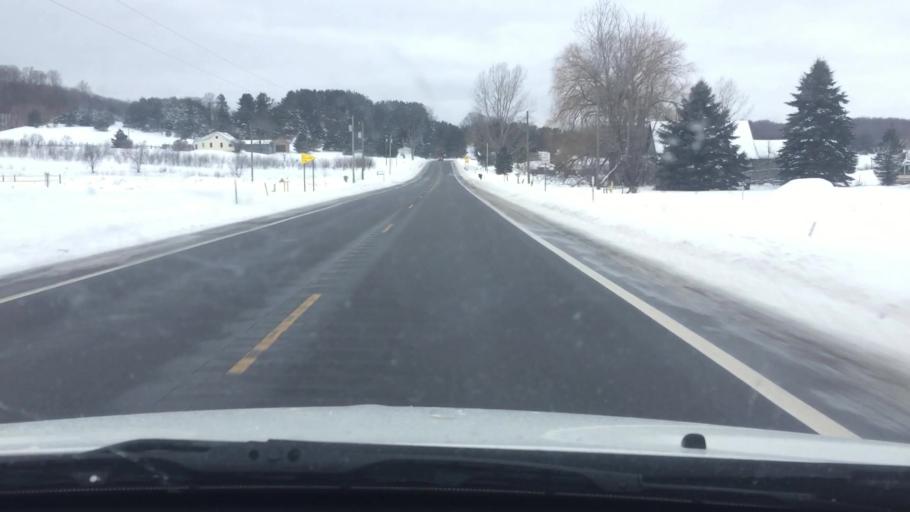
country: US
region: Michigan
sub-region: Charlevoix County
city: East Jordan
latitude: 45.1035
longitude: -85.0439
